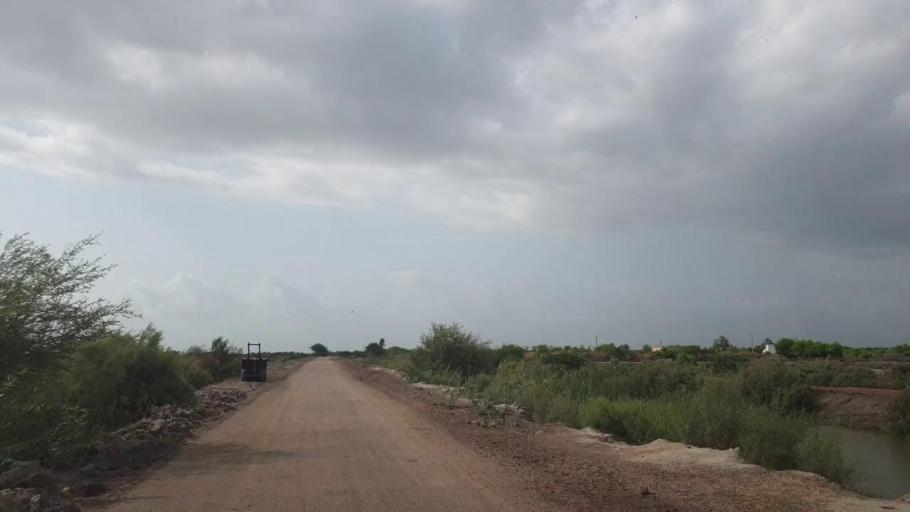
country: PK
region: Sindh
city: Kadhan
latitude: 24.5765
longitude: 69.0597
